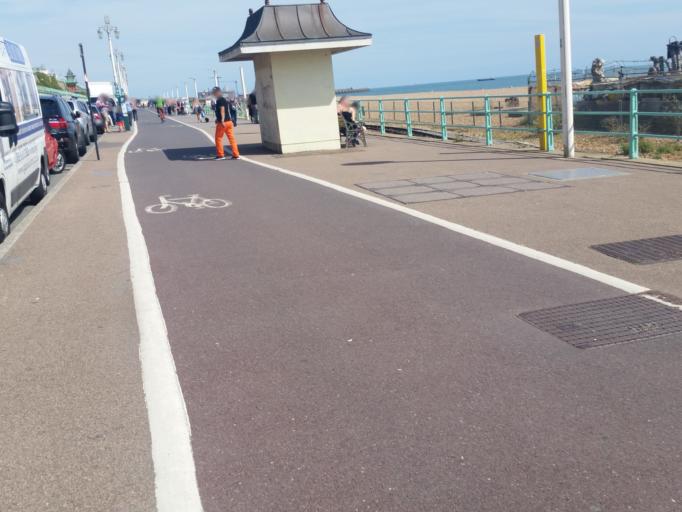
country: GB
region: England
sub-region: Brighton and Hove
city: Brighton
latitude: 50.8183
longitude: -0.1285
